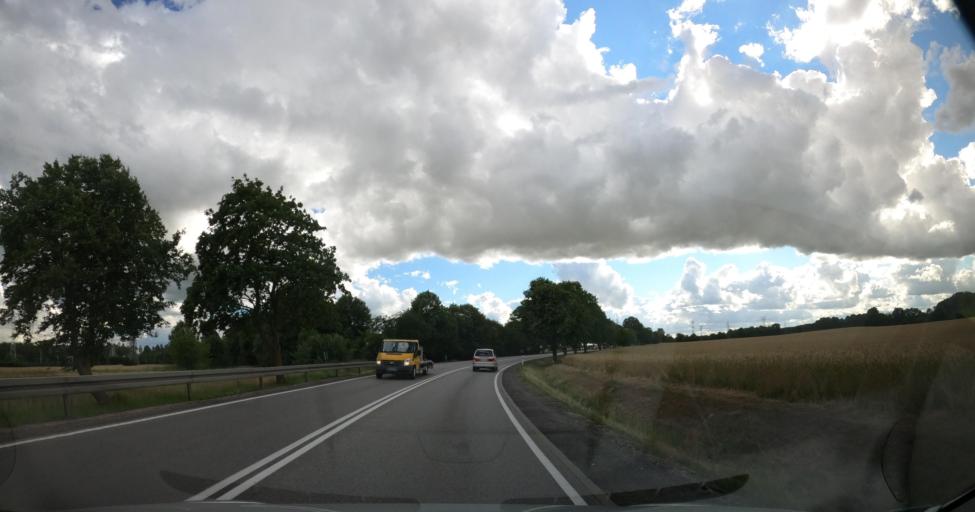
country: PL
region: Pomeranian Voivodeship
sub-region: Powiat kartuski
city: Banino
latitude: 54.3404
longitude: 18.4426
